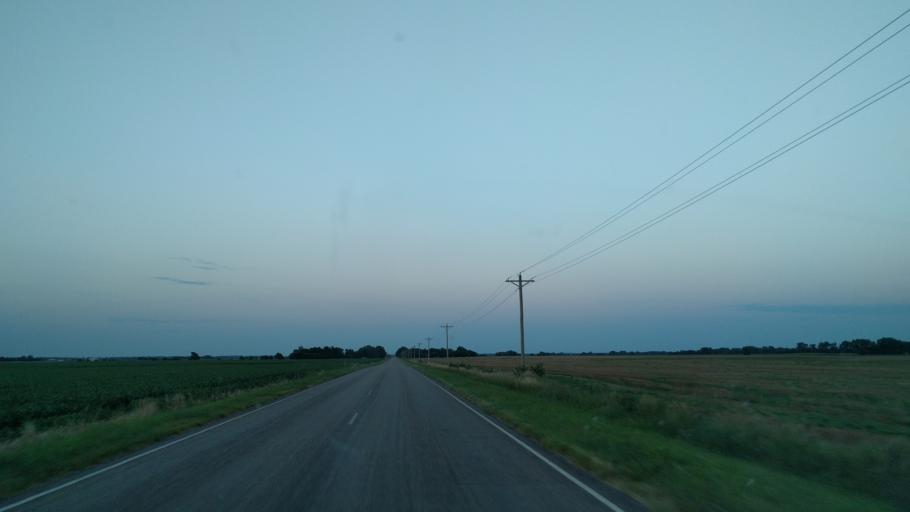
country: US
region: Kansas
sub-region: Rice County
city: Sterling
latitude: 38.2174
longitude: -98.1415
